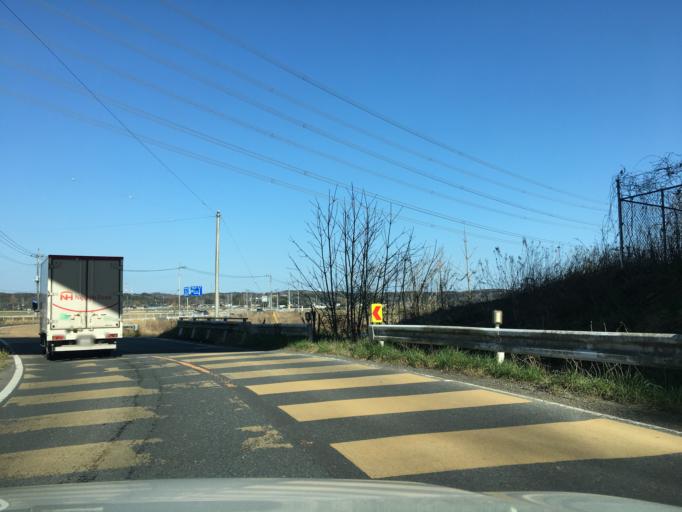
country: JP
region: Ibaraki
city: Omiya
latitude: 36.4868
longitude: 140.3806
